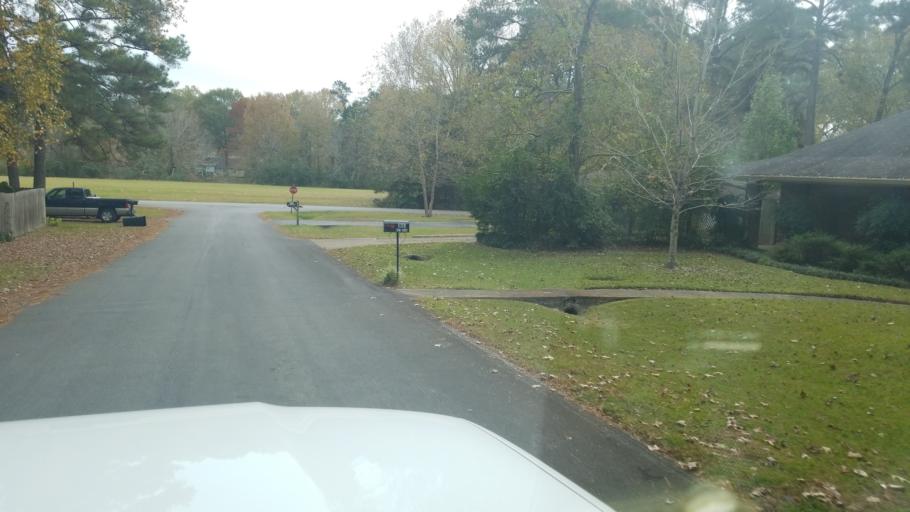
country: US
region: Mississippi
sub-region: Madison County
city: Ridgeland
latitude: 32.3842
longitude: -90.0318
